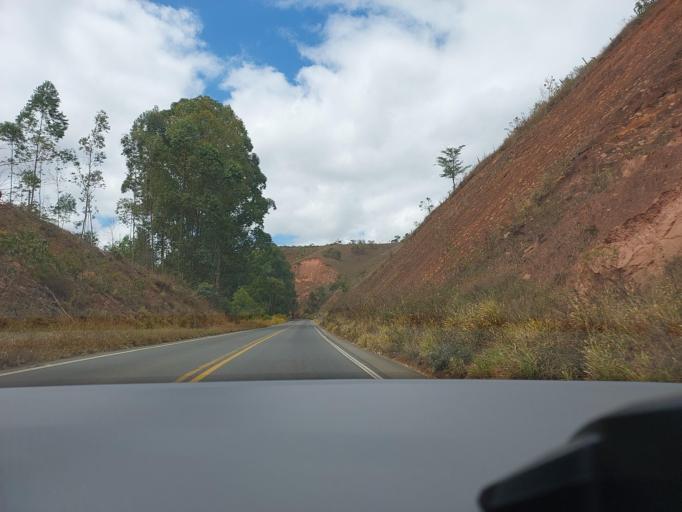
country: BR
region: Minas Gerais
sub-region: Vicosa
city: Vicosa
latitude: -20.8372
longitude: -42.7205
